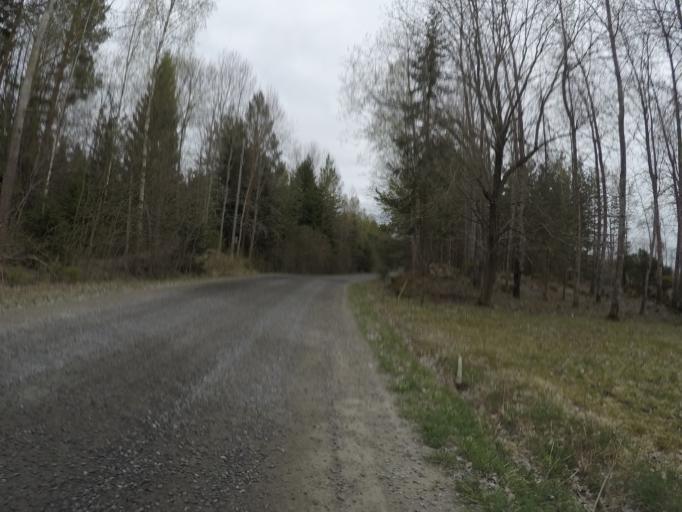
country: SE
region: Soedermanland
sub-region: Eskilstuna Kommun
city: Kvicksund
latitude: 59.3872
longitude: 16.3175
